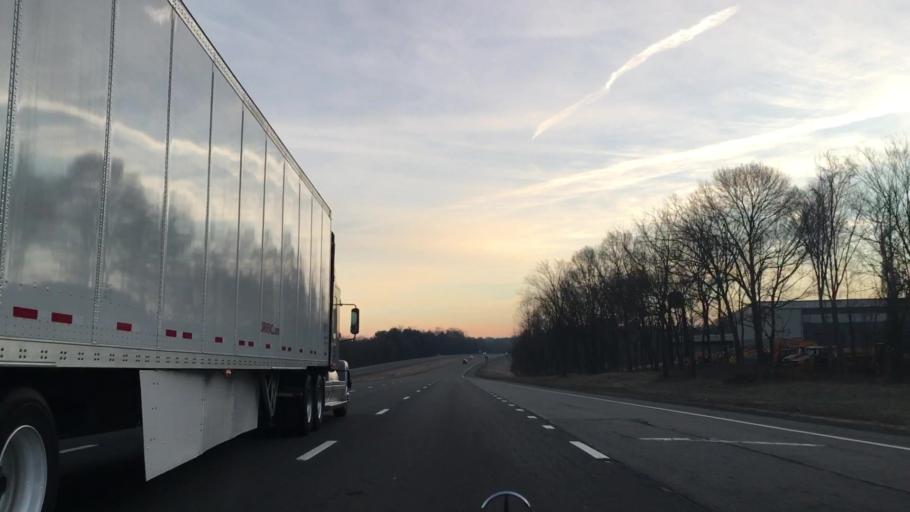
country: US
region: North Carolina
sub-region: Davidson County
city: Lexington
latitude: 35.7749
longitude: -80.3079
